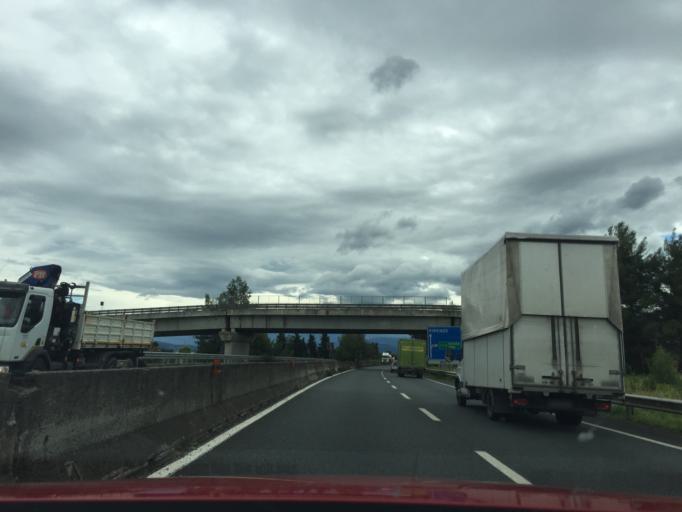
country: IT
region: Tuscany
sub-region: Province of Florence
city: Mantignano-Ugnano
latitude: 43.7741
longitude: 11.1549
